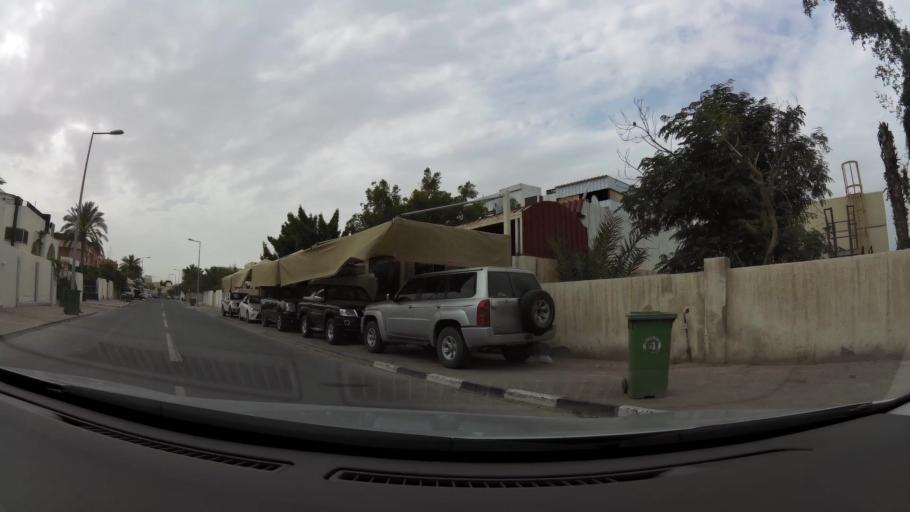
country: QA
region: Baladiyat ad Dawhah
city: Doha
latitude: 25.3349
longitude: 51.5053
